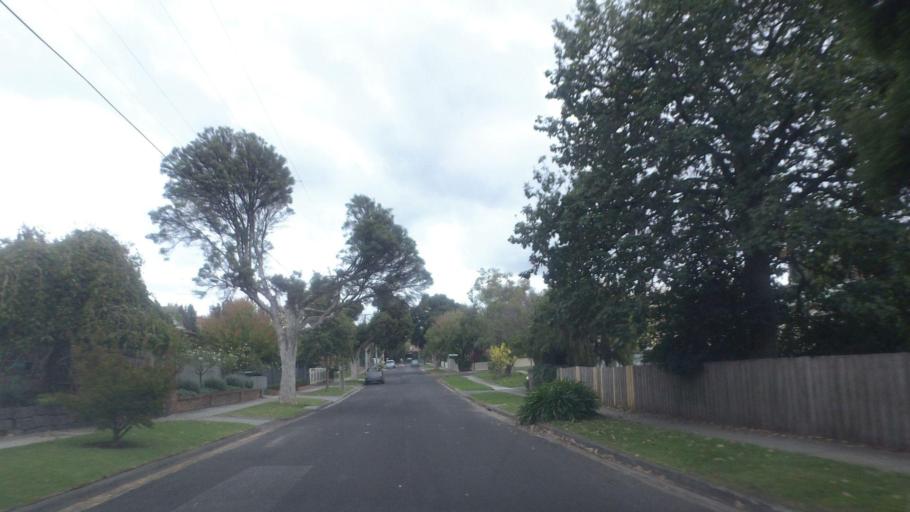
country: AU
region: Victoria
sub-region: Whitehorse
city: Box Hill South
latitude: -37.8272
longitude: 145.1241
